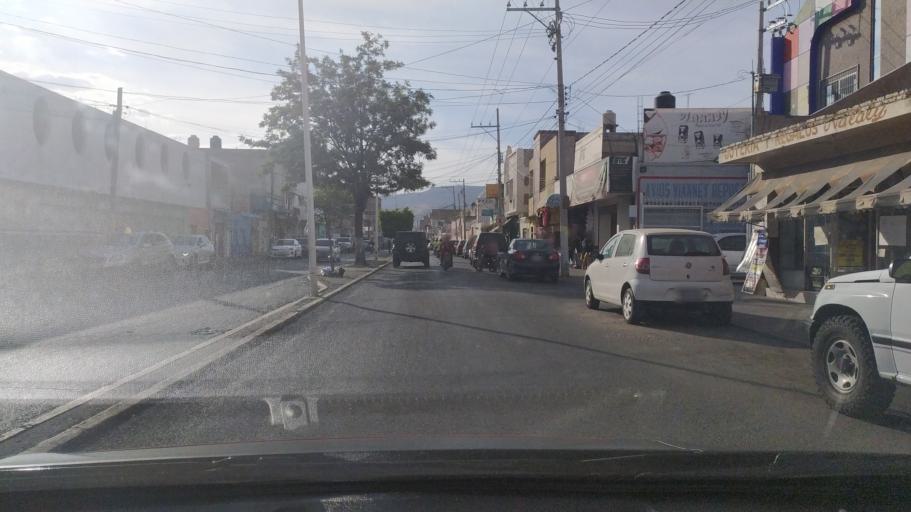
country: MX
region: Guanajuato
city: San Francisco del Rincon
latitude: 21.0159
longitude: -101.8553
